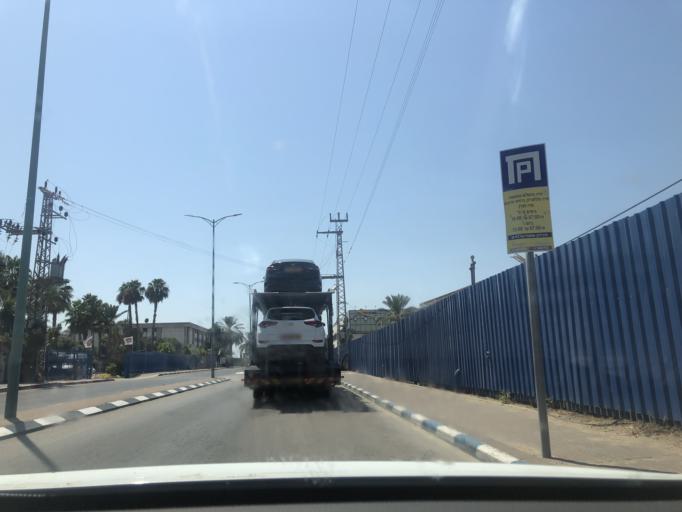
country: IL
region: Central District
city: Lod
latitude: 31.9690
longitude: 34.8958
